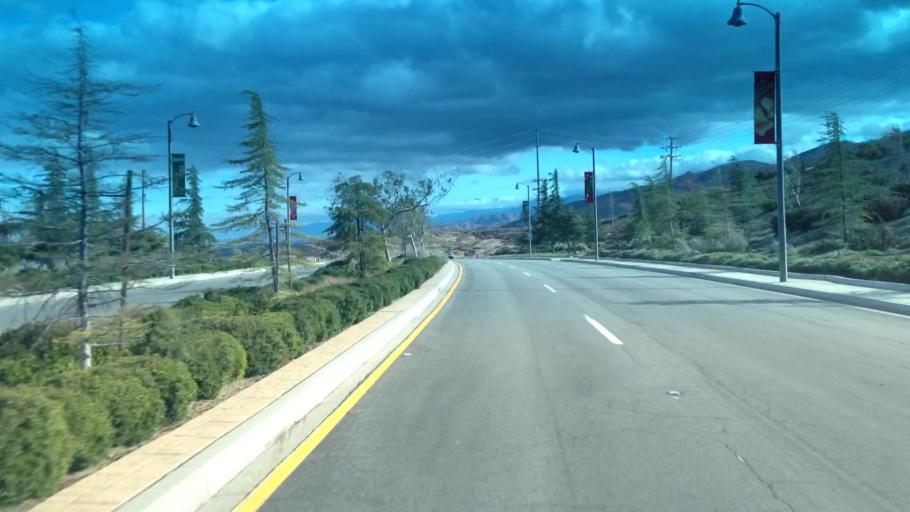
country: US
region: California
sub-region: Los Angeles County
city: Desert View Highlands
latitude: 34.5594
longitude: -118.1663
